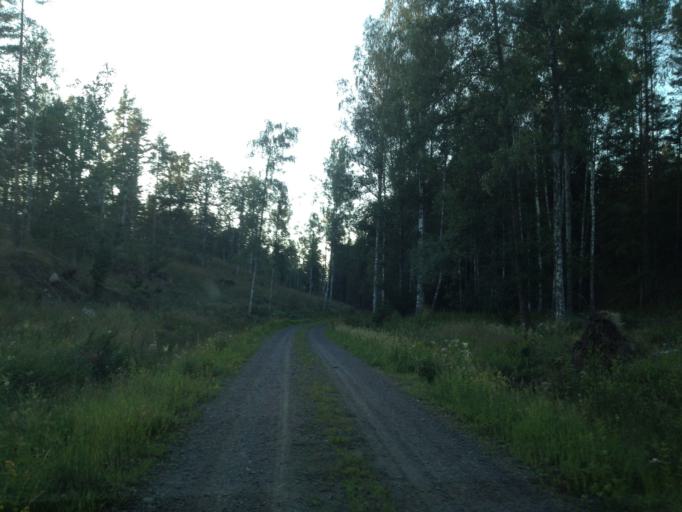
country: SE
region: Kalmar
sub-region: Vasterviks Kommun
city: Overum
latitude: 58.0143
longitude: 16.1196
